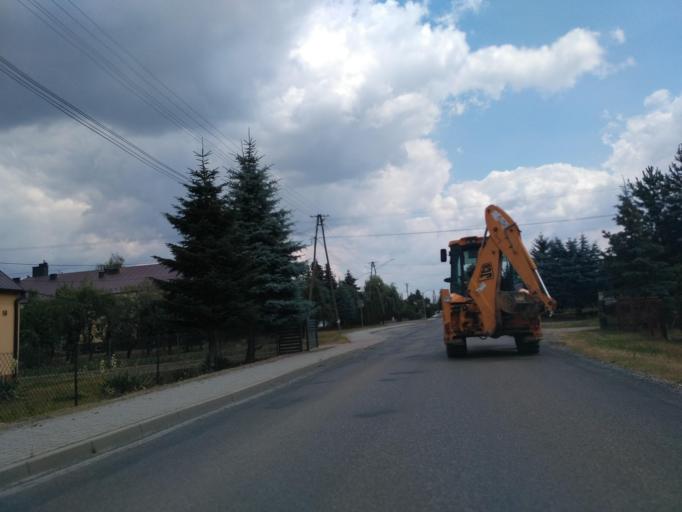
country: PL
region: Subcarpathian Voivodeship
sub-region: Powiat debicki
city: Zyrakow
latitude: 50.0477
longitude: 21.3393
